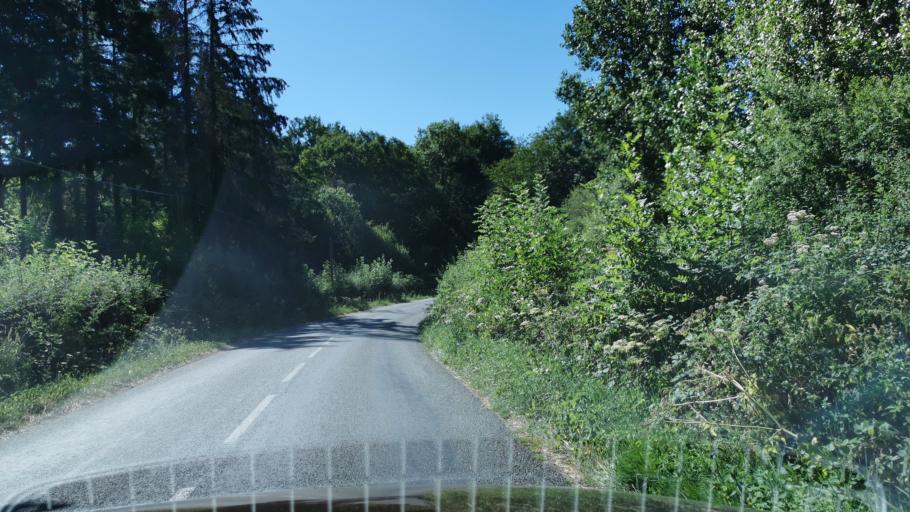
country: FR
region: Bourgogne
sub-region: Departement de Saone-et-Loire
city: Torcy
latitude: 46.7708
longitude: 4.4714
